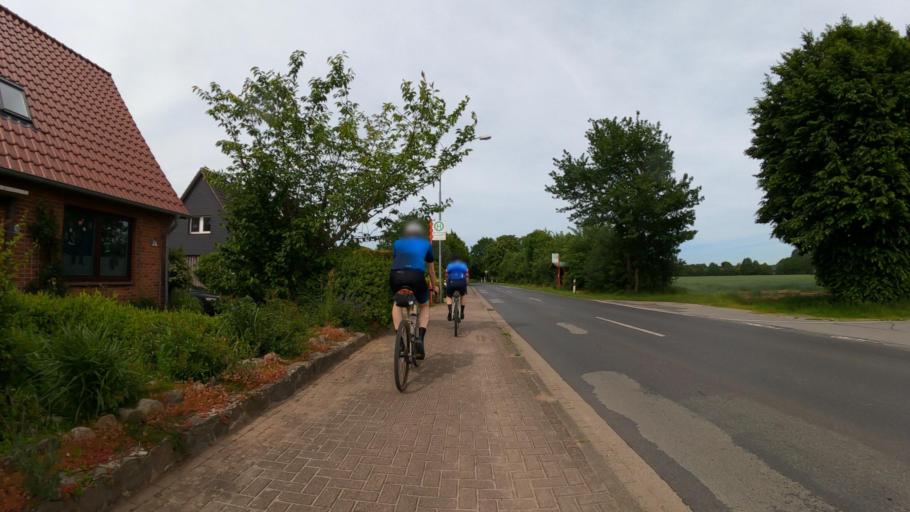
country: DE
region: Schleswig-Holstein
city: Sievershutten
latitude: 53.8396
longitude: 10.0932
